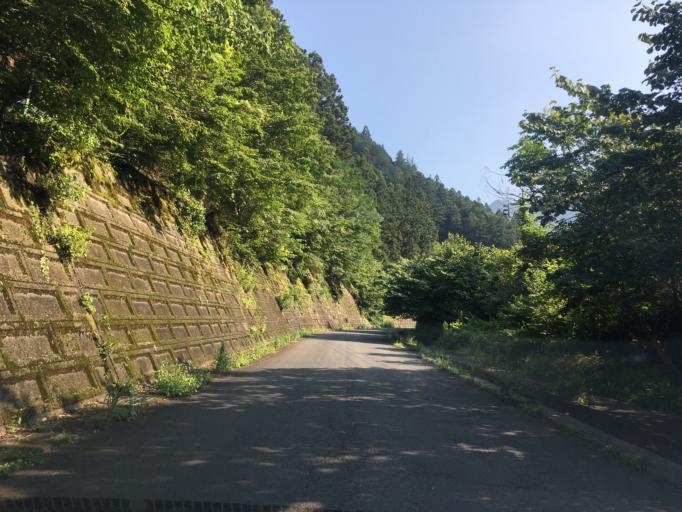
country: JP
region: Saitama
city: Chichibu
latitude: 35.9487
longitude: 139.1183
